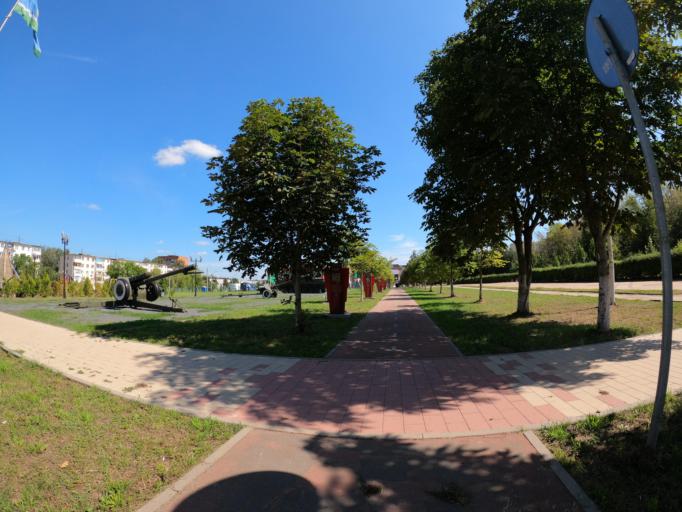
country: RU
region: Moskovskaya
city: Stupino
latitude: 54.8901
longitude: 38.0827
